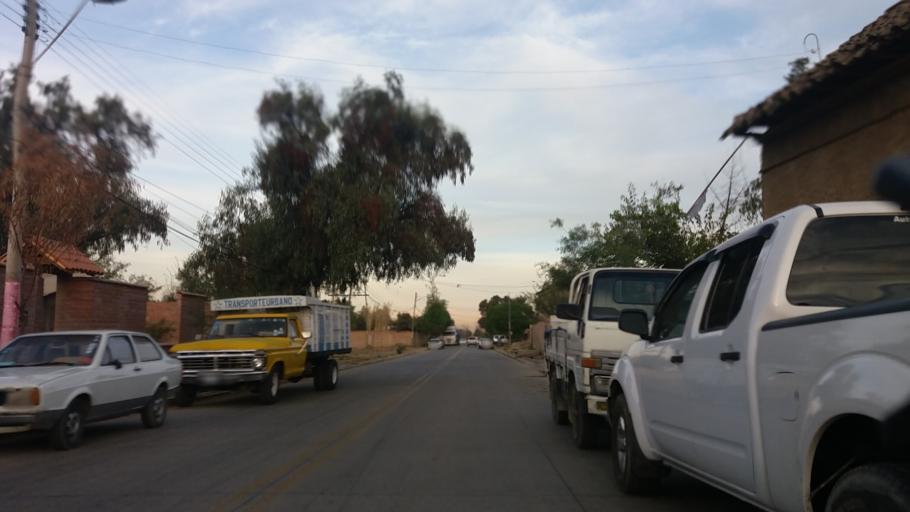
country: BO
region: Cochabamba
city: Cochabamba
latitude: -17.3673
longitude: -66.2135
